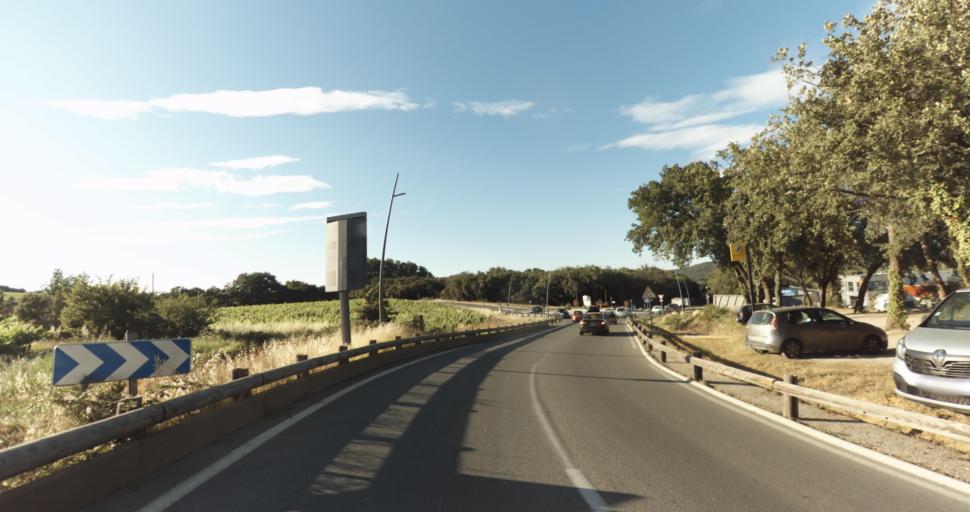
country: FR
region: Provence-Alpes-Cote d'Azur
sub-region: Departement du Var
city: La Croix-Valmer
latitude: 43.2135
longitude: 6.5672
